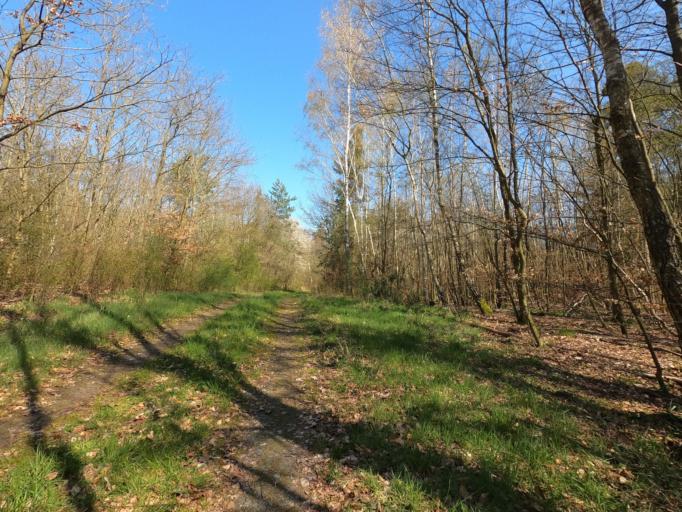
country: DE
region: Hesse
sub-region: Regierungsbezirk Darmstadt
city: Buttelborn
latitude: 49.9466
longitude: 8.5343
